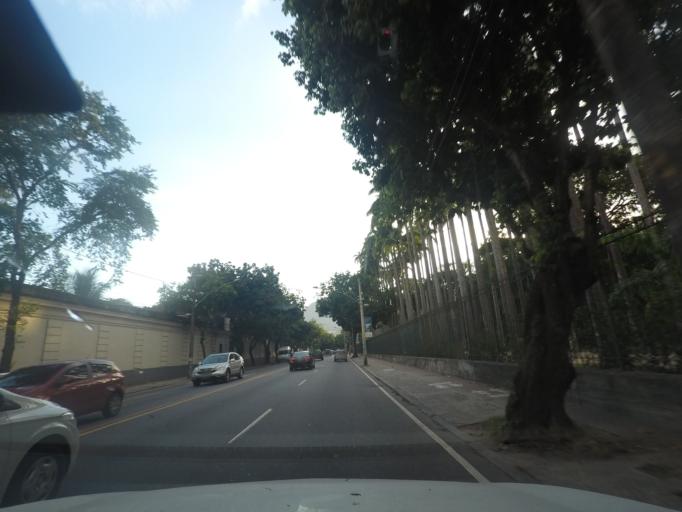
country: BR
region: Rio de Janeiro
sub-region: Rio De Janeiro
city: Rio de Janeiro
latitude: -22.9689
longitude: -43.2218
